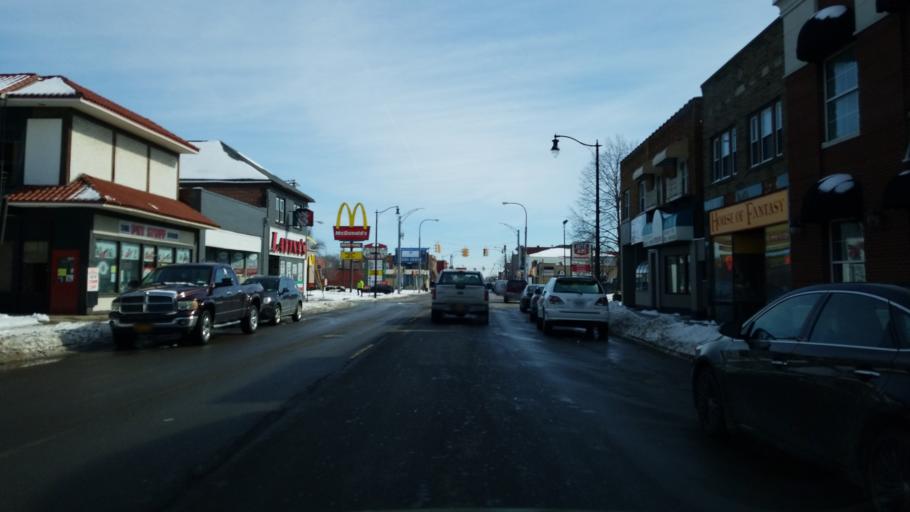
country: US
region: New York
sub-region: Niagara County
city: Niagara Falls
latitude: 43.0951
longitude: -79.0414
